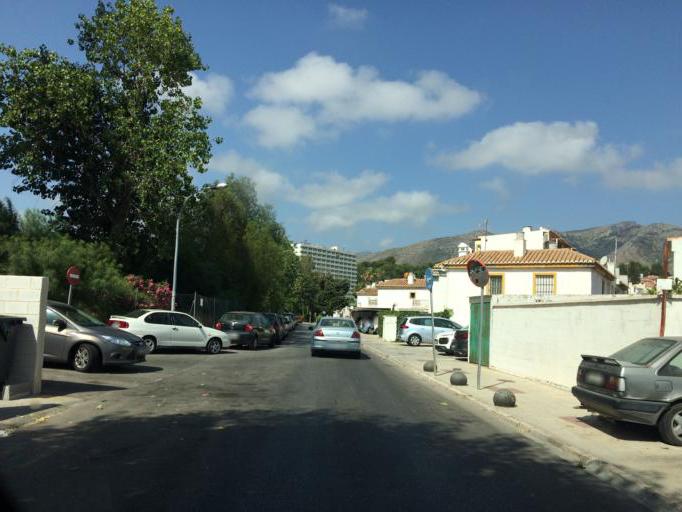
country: ES
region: Andalusia
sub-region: Provincia de Malaga
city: Torremolinos
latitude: 36.6400
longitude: -4.4946
